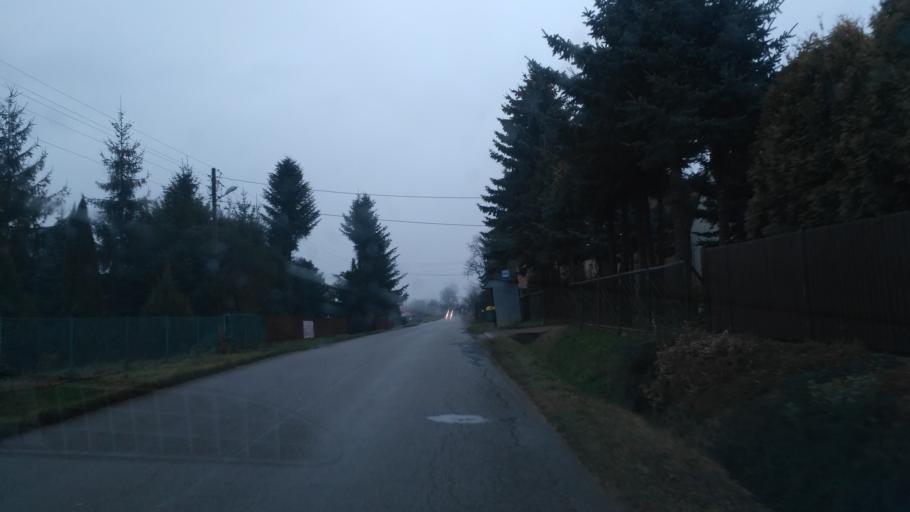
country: PL
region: Subcarpathian Voivodeship
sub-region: Powiat jaroslawski
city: Rokietnica
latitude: 49.9459
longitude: 22.6097
